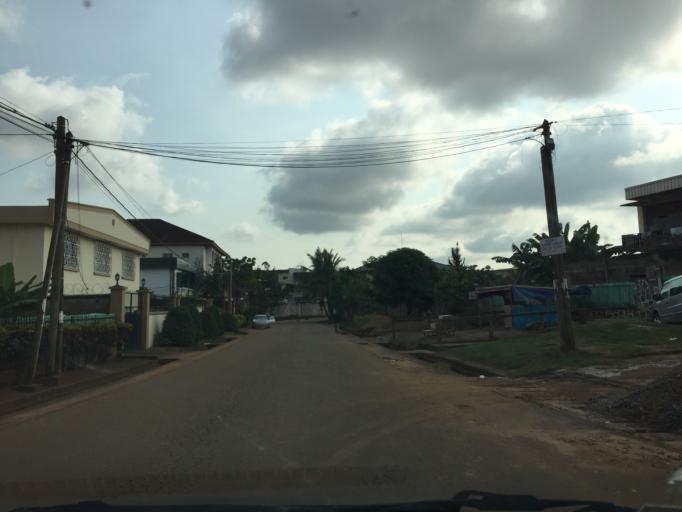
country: CM
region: Centre
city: Yaounde
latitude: 3.8836
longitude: 11.5152
